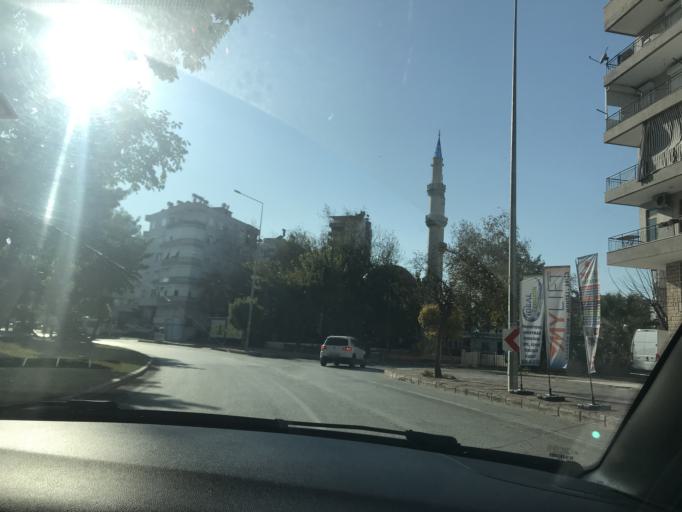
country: TR
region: Antalya
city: Antalya
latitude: 36.9035
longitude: 30.7024
